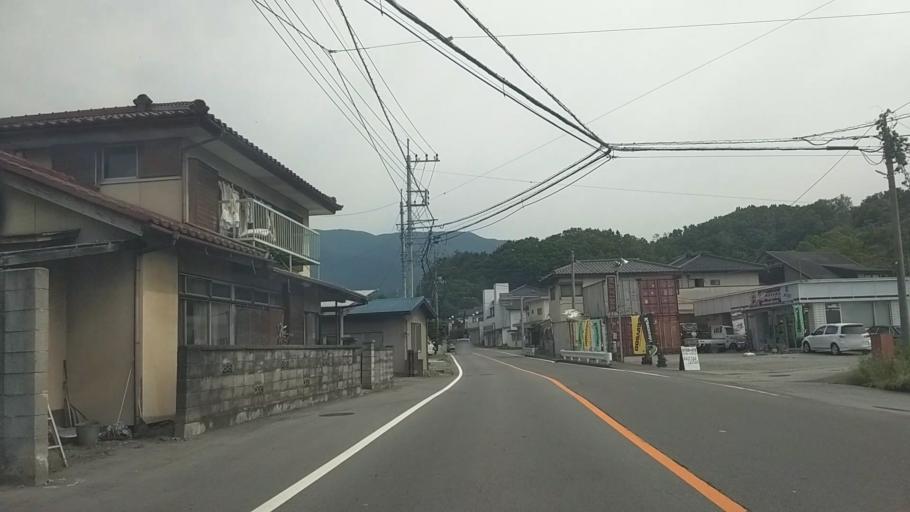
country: JP
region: Yamanashi
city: Isawa
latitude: 35.5950
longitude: 138.5877
